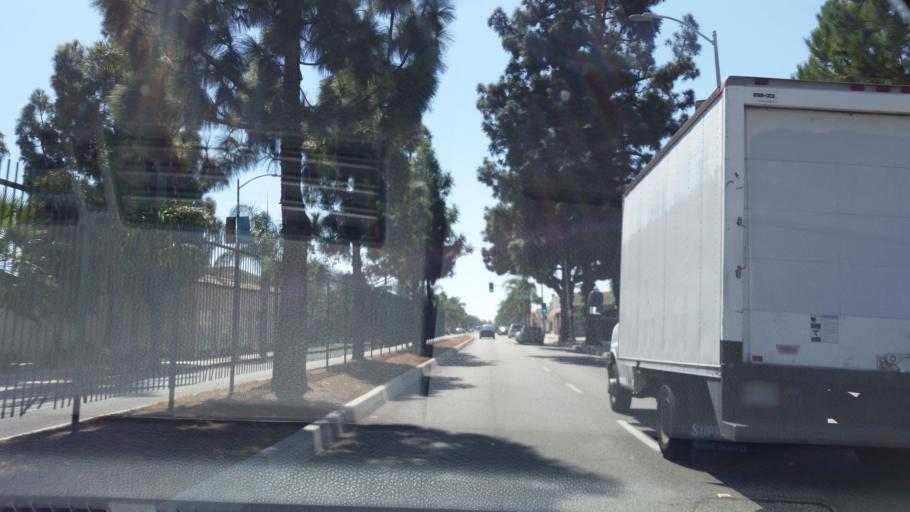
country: US
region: California
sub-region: Orange County
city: Santa Ana
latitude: 33.7334
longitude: -117.8679
